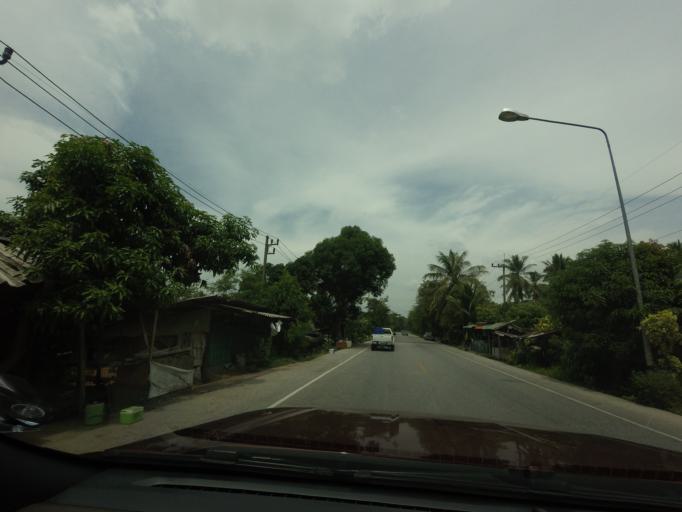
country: TH
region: Yala
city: Yala
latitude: 6.6134
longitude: 101.3063
